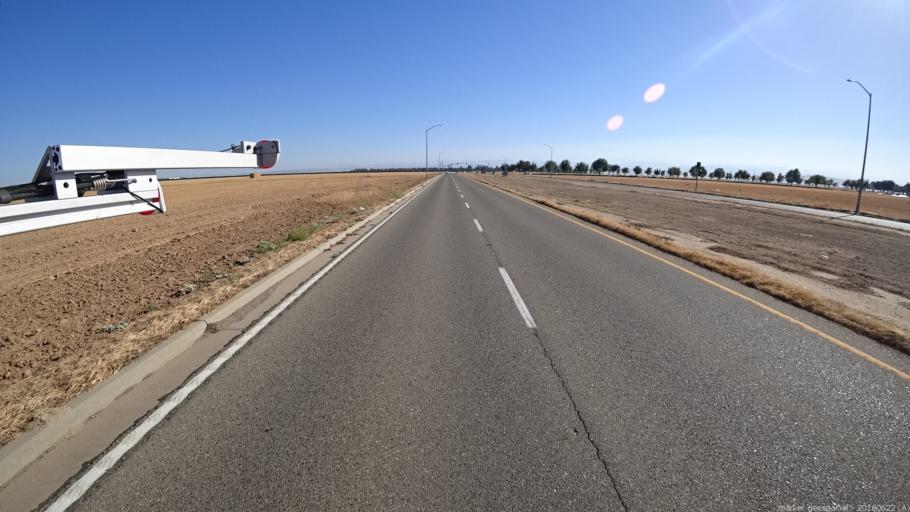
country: US
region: California
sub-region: Fresno County
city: Clovis
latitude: 36.8857
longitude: -119.8059
